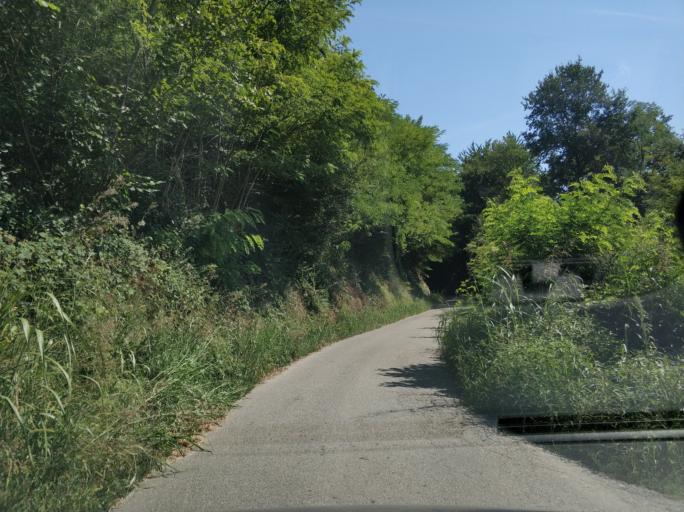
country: IT
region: Piedmont
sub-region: Provincia di Torino
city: San Maurizio
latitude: 45.2335
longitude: 7.6298
